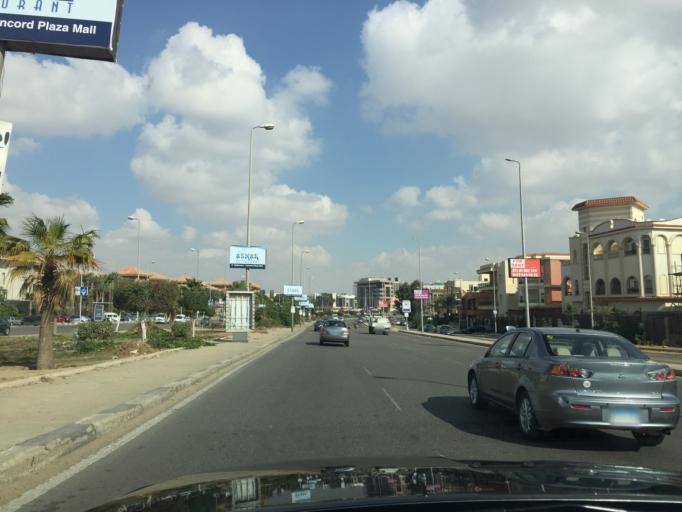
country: EG
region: Muhafazat al Qalyubiyah
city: Al Khankah
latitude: 30.0232
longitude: 31.4539
